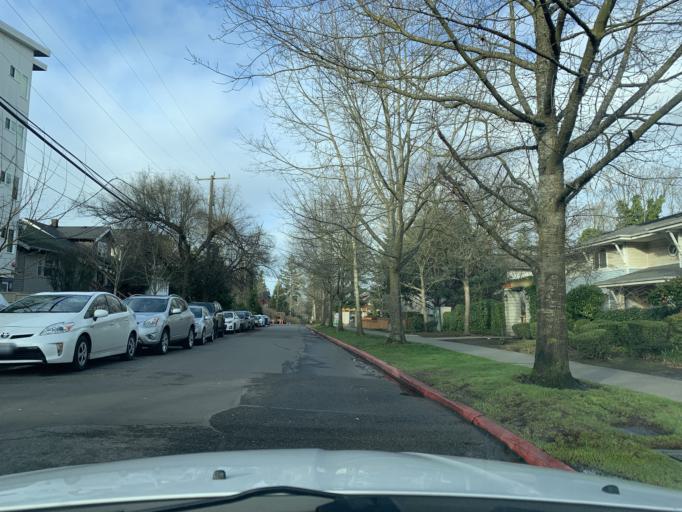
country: US
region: Washington
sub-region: King County
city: Seattle
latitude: 47.6641
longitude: -122.3054
